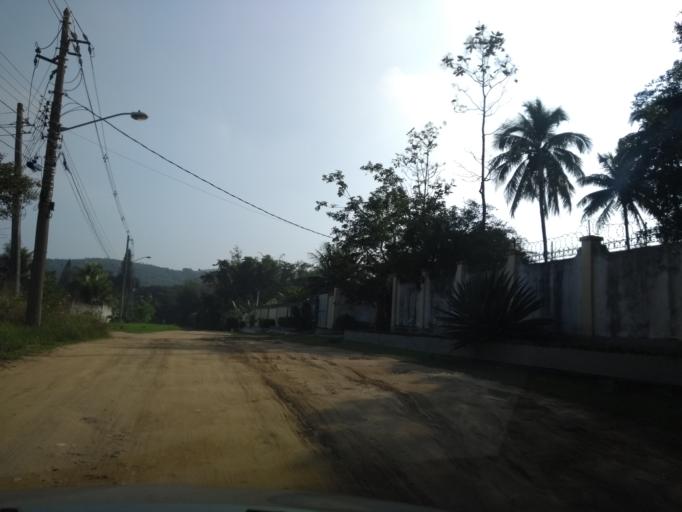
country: BR
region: Rio de Janeiro
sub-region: Itaguai
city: Itaguai
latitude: -22.9667
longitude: -43.6379
